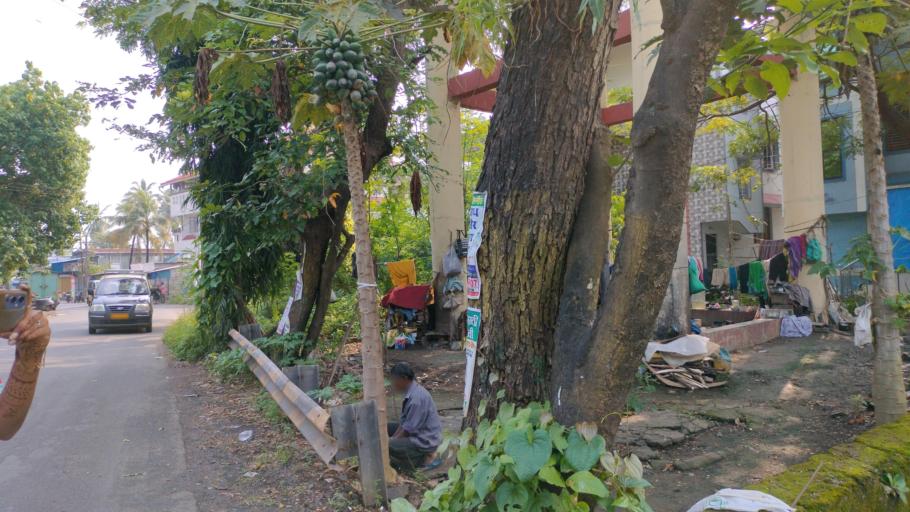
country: IN
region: Maharashtra
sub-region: Thane
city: Virar
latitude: 19.4432
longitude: 72.7763
